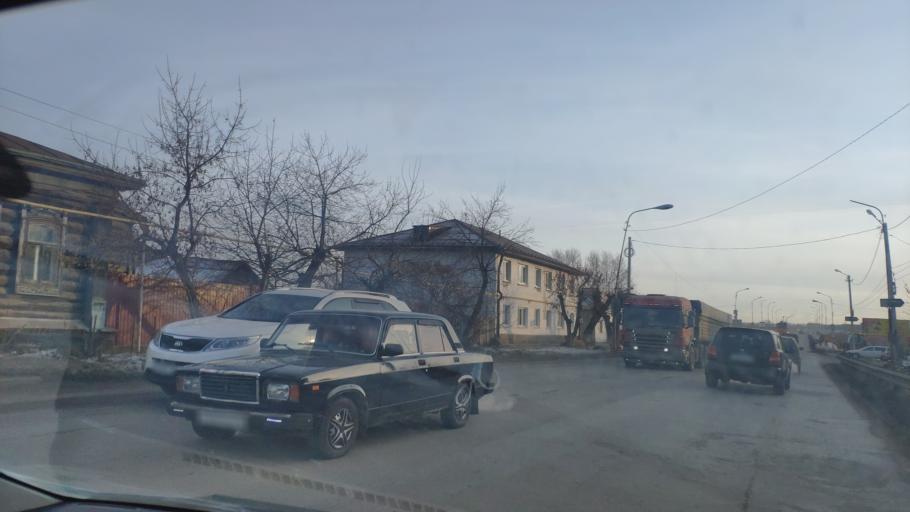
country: RU
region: Kurgan
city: Shadrinsk
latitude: 56.0783
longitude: 63.6410
